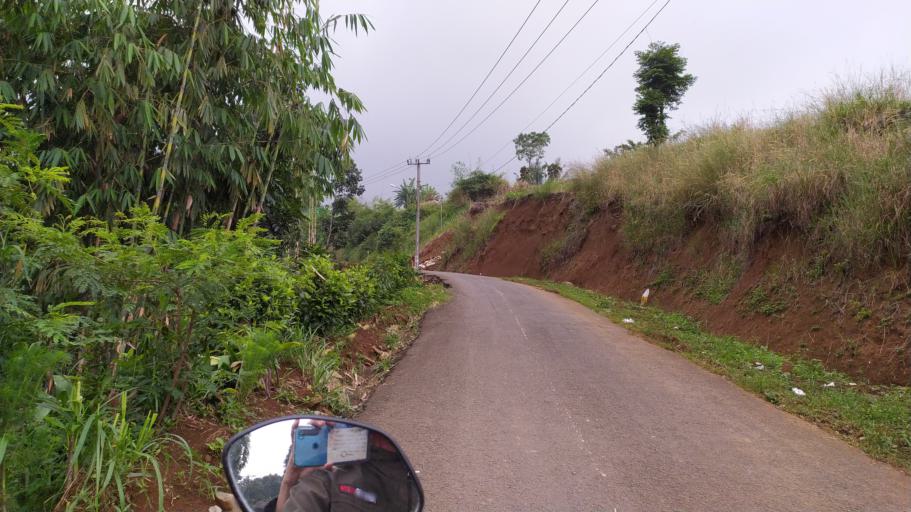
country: ID
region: West Java
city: Ciampea
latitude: -6.6444
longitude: 106.7045
